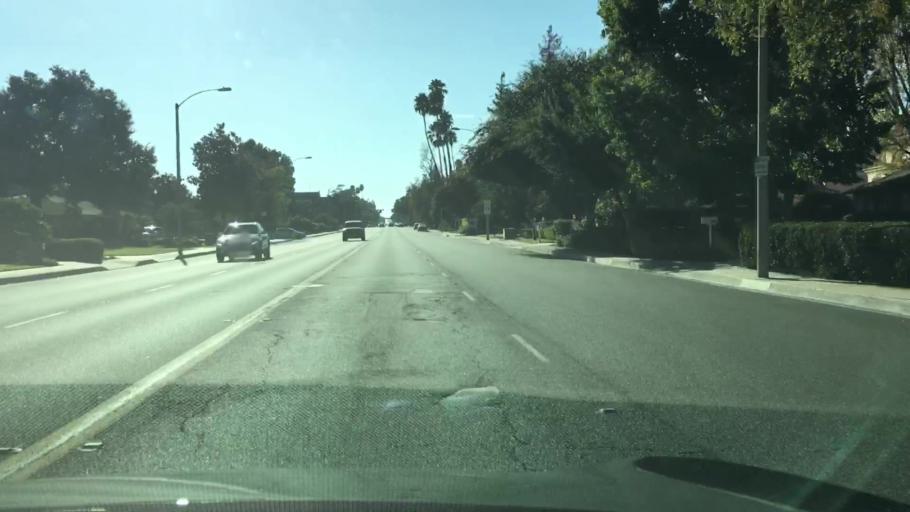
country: US
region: California
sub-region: Los Angeles County
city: Arcadia
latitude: 34.1280
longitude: -118.0421
